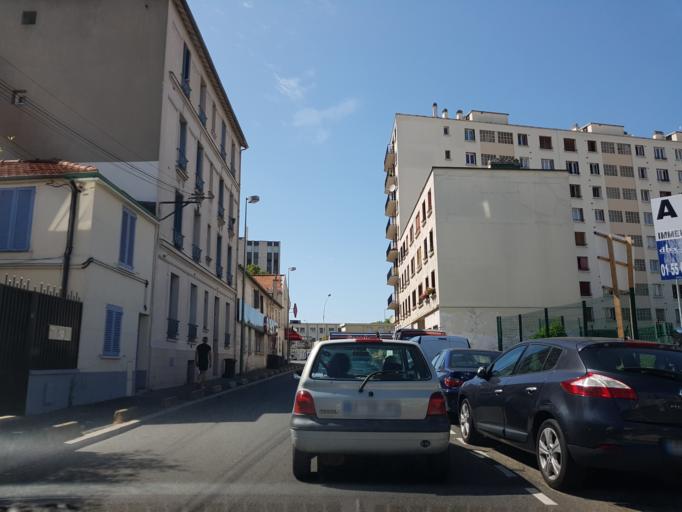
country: FR
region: Ile-de-France
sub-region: Departement du Val-de-Marne
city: Arcueil
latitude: 48.8055
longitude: 2.3265
